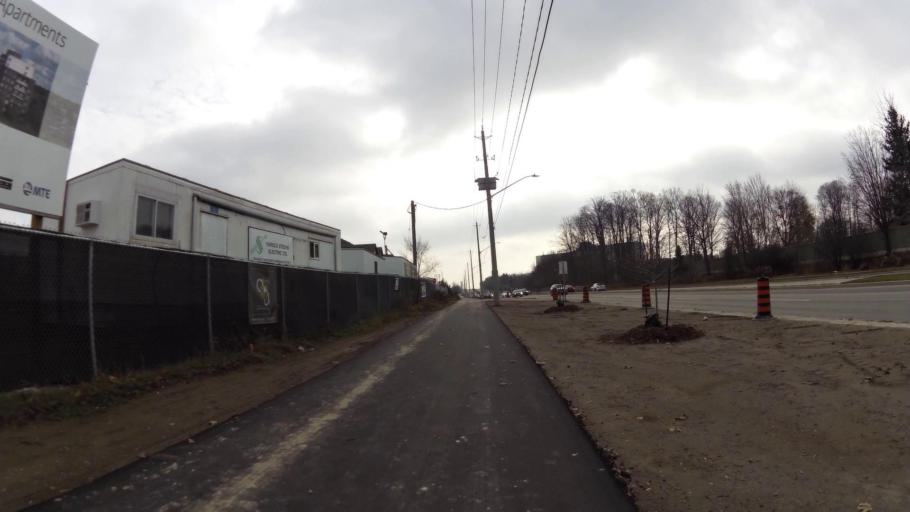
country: CA
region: Ontario
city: Kitchener
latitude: 43.4173
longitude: -80.4699
